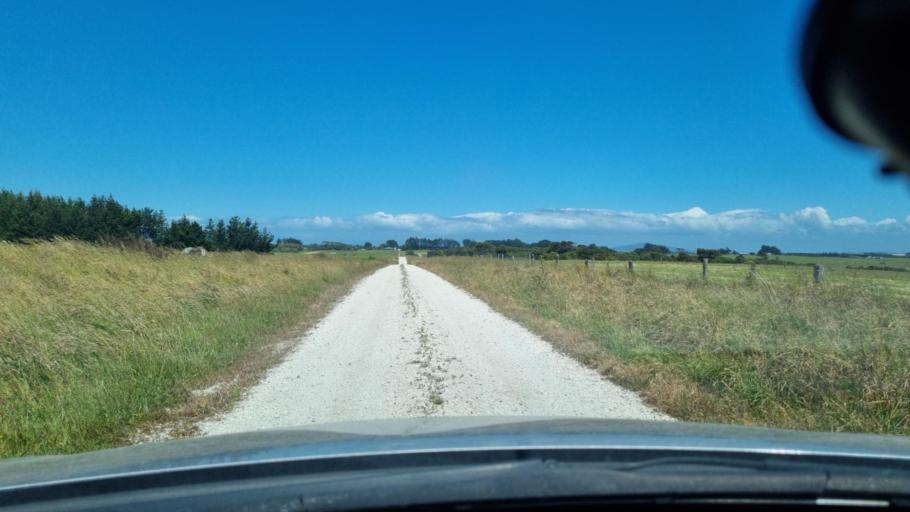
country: NZ
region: Southland
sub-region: Invercargill City
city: Invercargill
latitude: -46.4601
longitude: 168.4201
